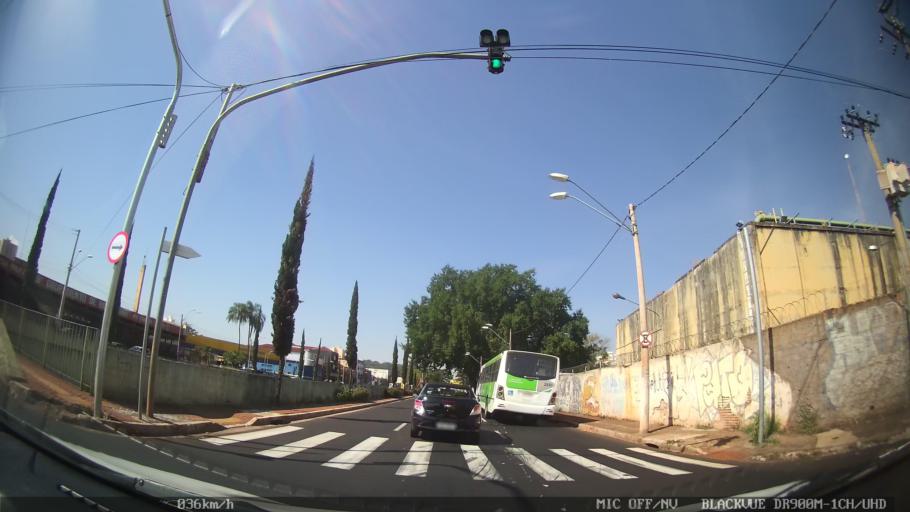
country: BR
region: Sao Paulo
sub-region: Ribeirao Preto
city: Ribeirao Preto
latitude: -21.1682
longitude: -47.8131
